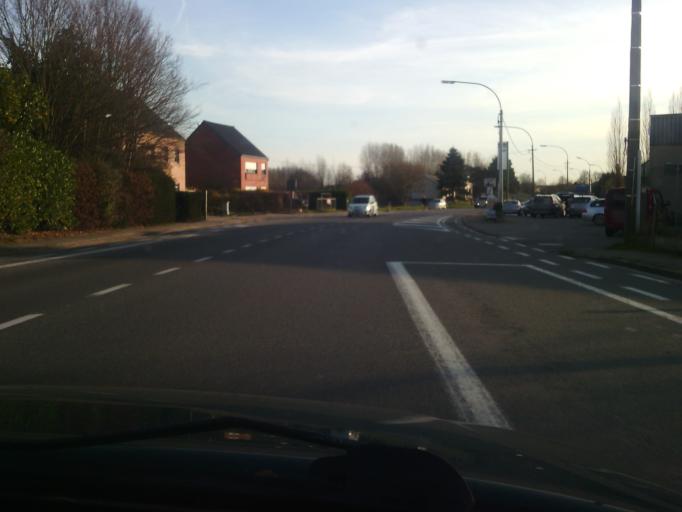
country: BE
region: Flanders
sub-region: Provincie Oost-Vlaanderen
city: Berlare
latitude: 51.0093
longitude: 4.0081
